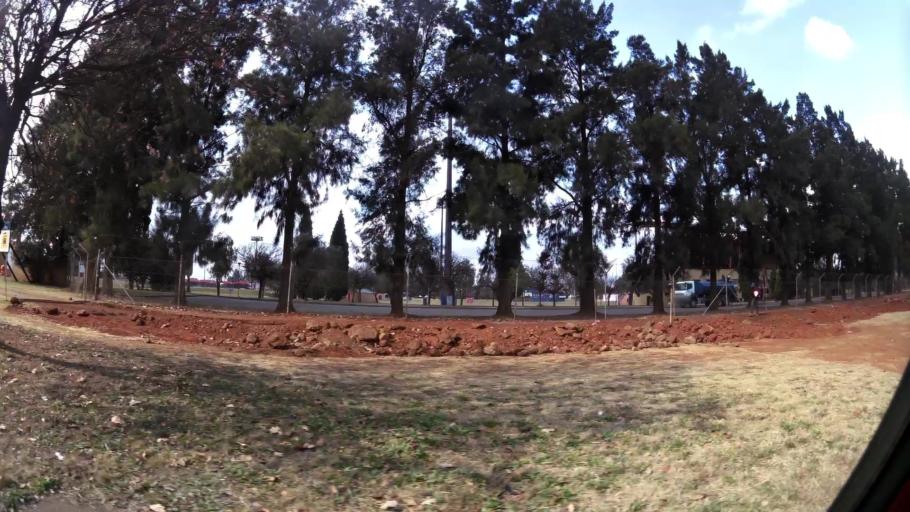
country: ZA
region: Gauteng
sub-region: Sedibeng District Municipality
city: Vanderbijlpark
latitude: -26.7043
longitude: 27.8593
